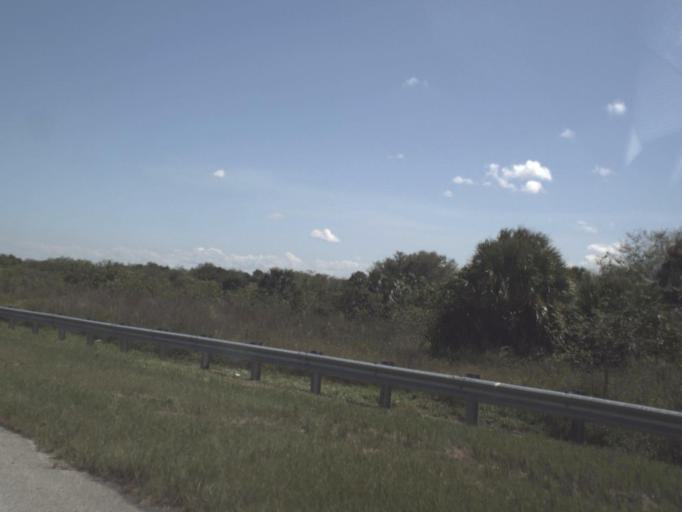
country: US
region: Florida
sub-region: Glades County
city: Moore Haven
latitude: 26.8127
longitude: -81.2059
